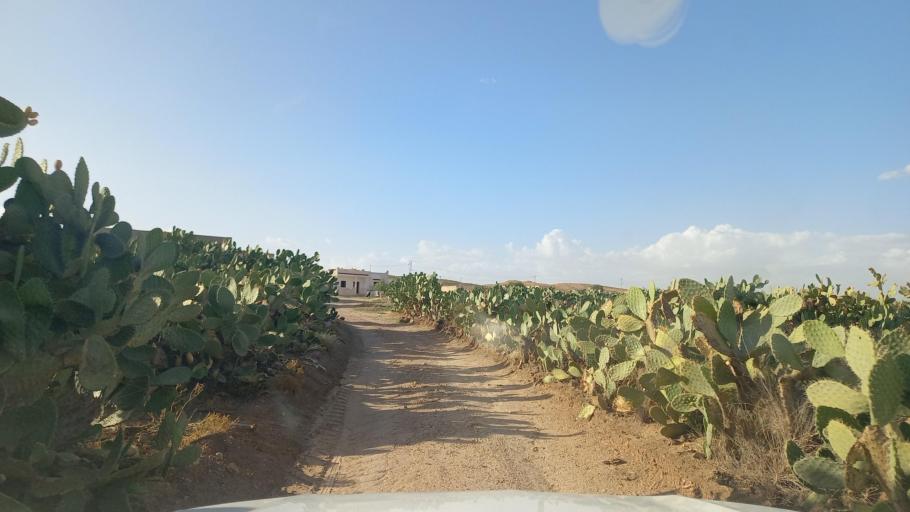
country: TN
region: Al Qasrayn
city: Sbiba
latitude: 35.3651
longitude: 9.0046
